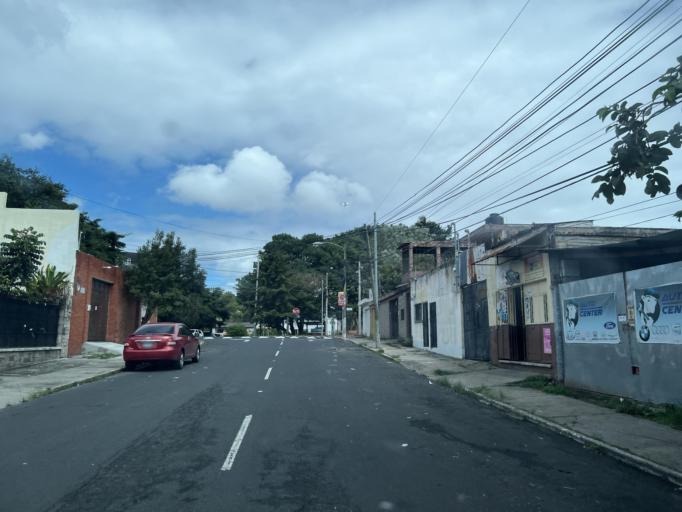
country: GT
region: Guatemala
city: Guatemala City
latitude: 14.6099
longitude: -90.5011
